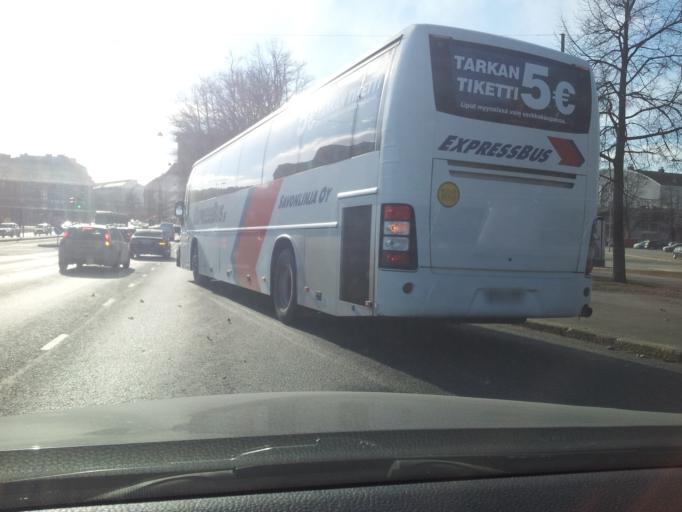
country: FI
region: Uusimaa
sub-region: Helsinki
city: Helsinki
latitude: 60.1828
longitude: 24.9299
